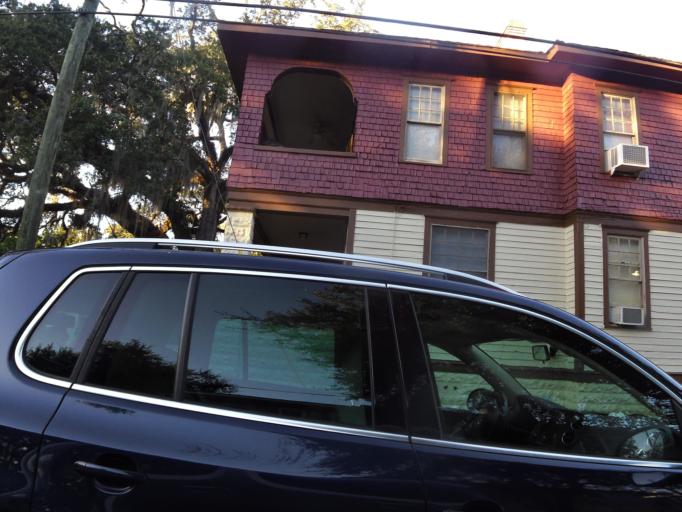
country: US
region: Florida
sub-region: Duval County
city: Jacksonville
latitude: 30.3403
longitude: -81.6528
